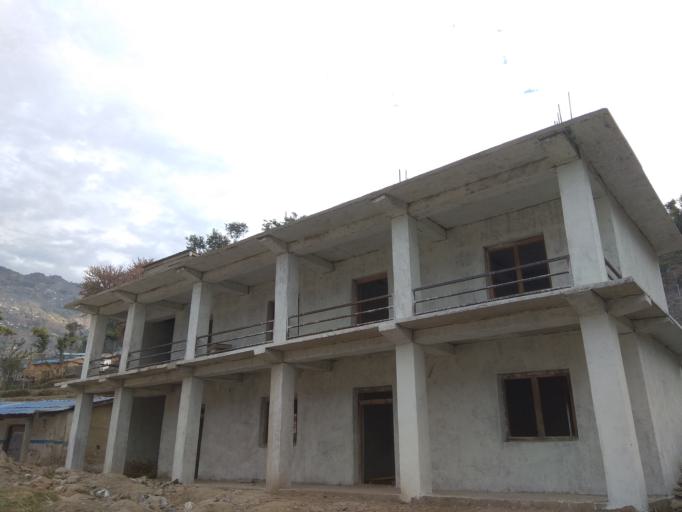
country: NP
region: Far Western
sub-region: Seti Zone
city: Achham
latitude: 29.2368
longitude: 81.6289
